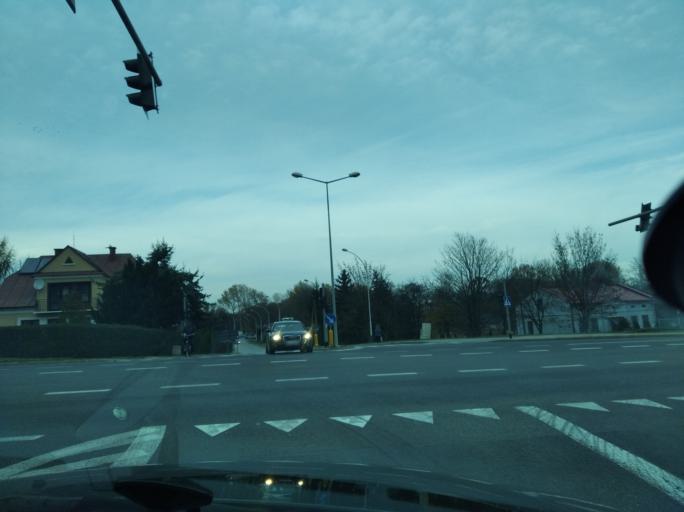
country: PL
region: Subcarpathian Voivodeship
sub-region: Powiat przeworski
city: Przeworsk
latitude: 50.0605
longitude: 22.4795
